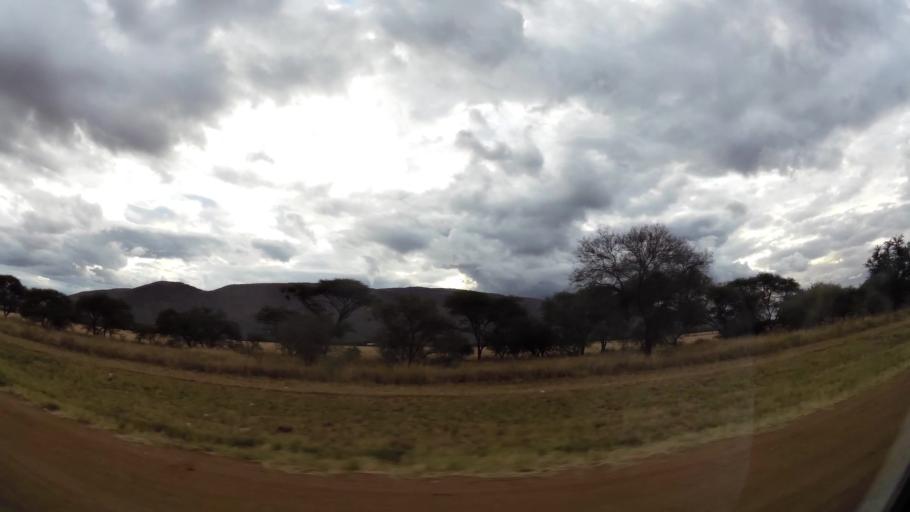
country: ZA
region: Limpopo
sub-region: Waterberg District Municipality
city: Mokopane
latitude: -24.2471
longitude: 28.9920
